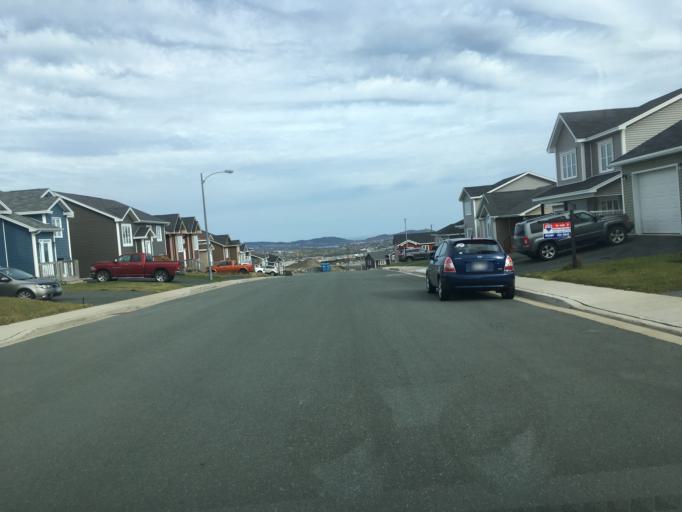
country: CA
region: Newfoundland and Labrador
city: Mount Pearl
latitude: 47.5515
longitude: -52.7872
